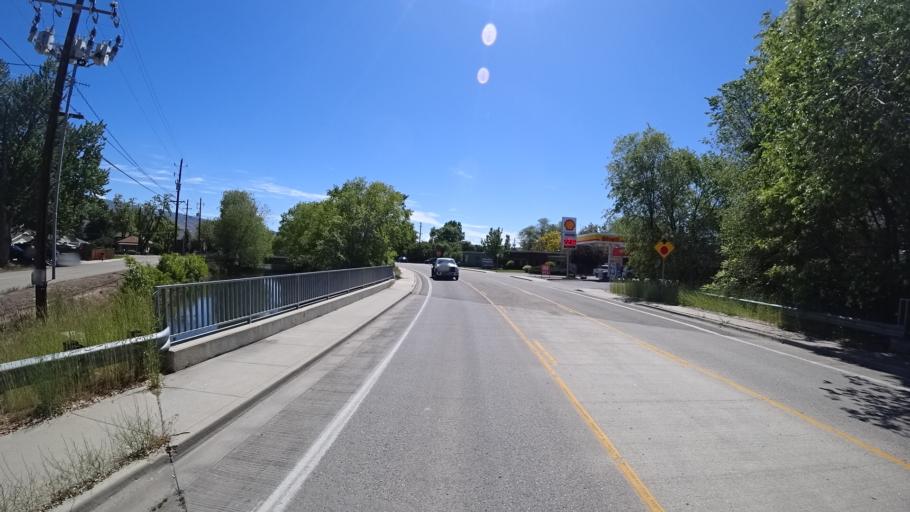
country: US
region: Idaho
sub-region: Ada County
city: Boise
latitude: 43.5745
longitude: -116.1647
